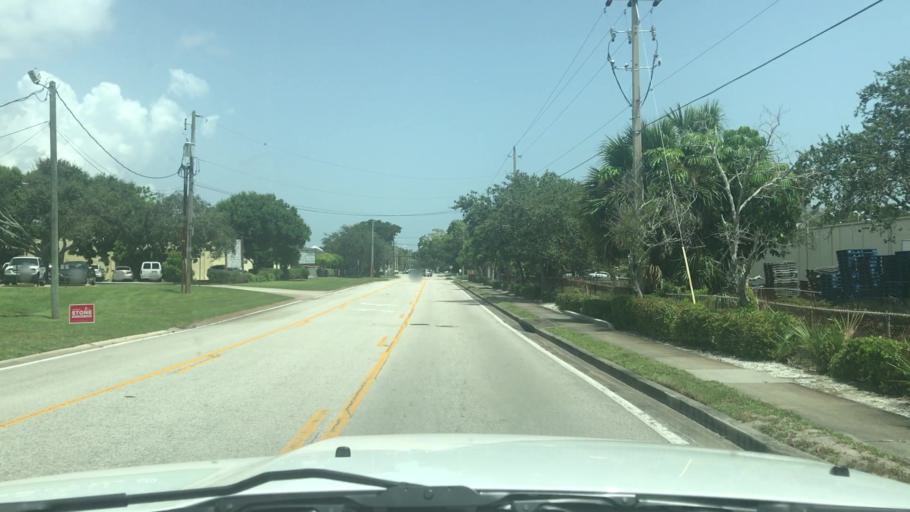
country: US
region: Florida
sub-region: Indian River County
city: Vero Beach
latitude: 27.6299
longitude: -80.3933
